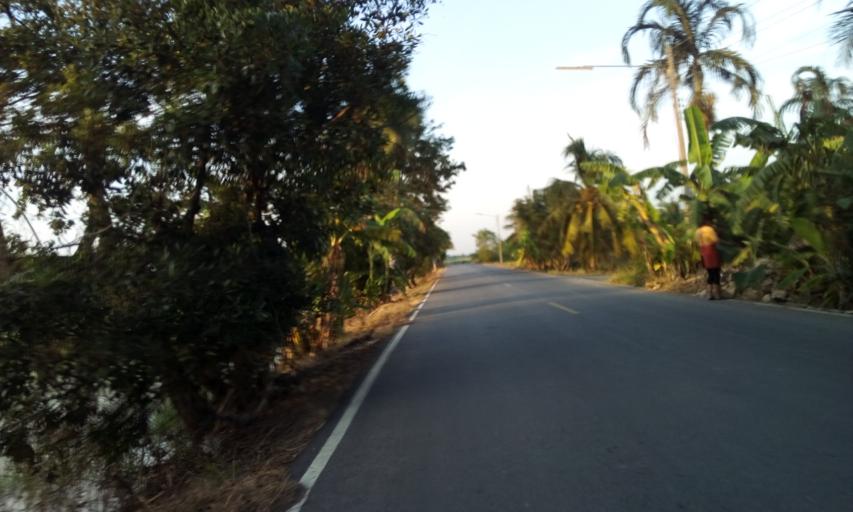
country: TH
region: Pathum Thani
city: Nong Suea
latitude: 14.0499
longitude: 100.8671
